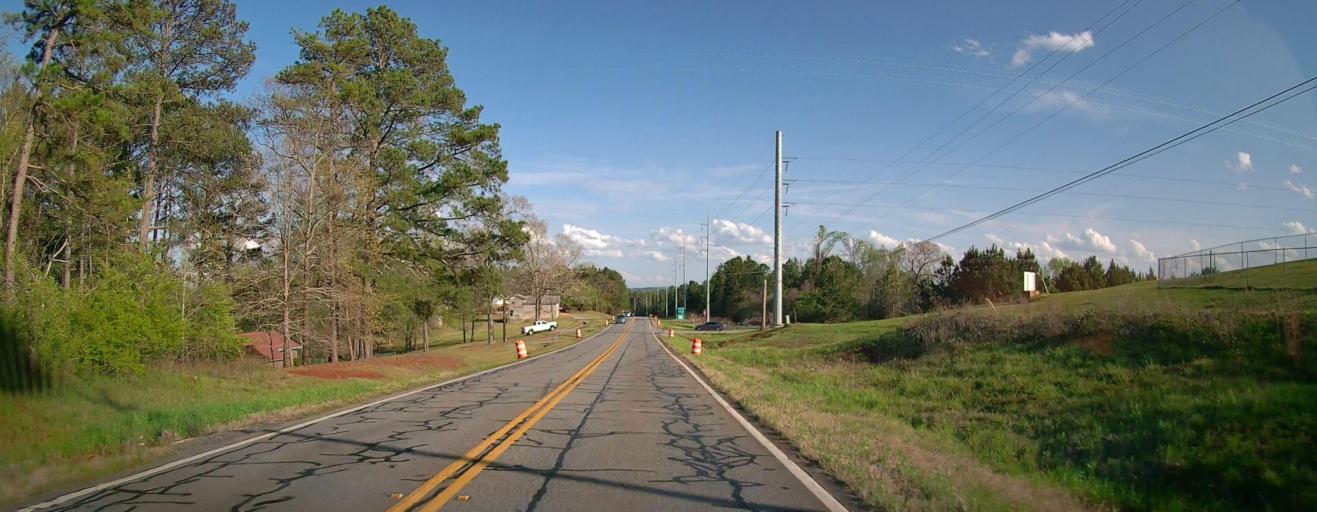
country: US
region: Georgia
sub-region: Baldwin County
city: Milledgeville
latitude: 33.1059
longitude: -83.2779
